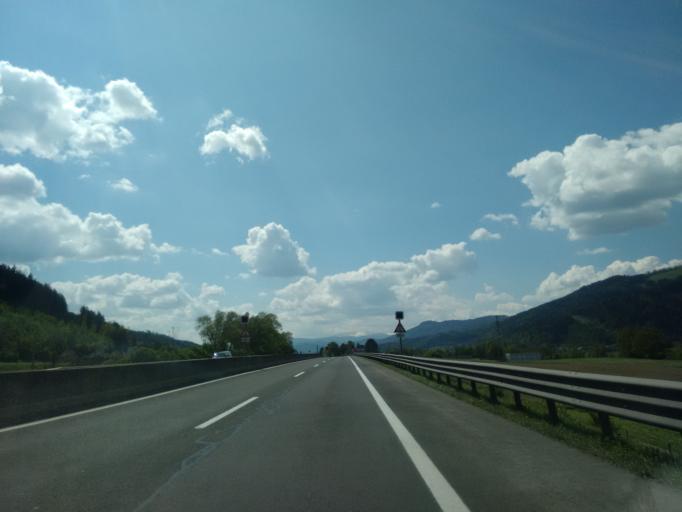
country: AT
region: Styria
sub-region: Politischer Bezirk Leoben
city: Niklasdorf
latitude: 47.4007
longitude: 15.1807
